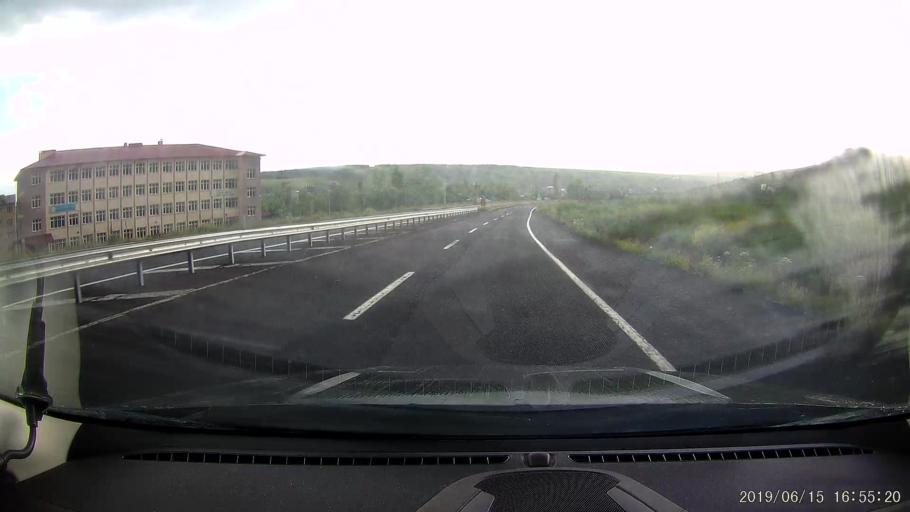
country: TR
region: Kars
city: Susuz
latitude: 40.7844
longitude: 43.1351
